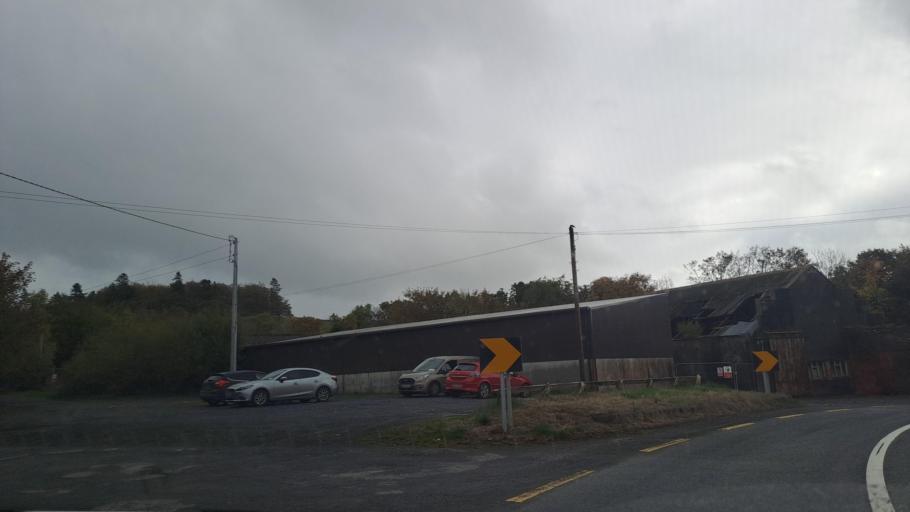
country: IE
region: Ulster
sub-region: An Cabhan
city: Bailieborough
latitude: 53.9277
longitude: -7.0037
